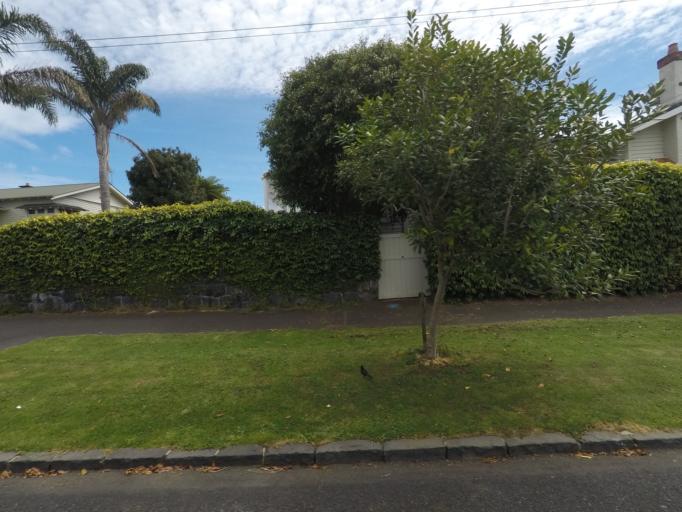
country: NZ
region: Auckland
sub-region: Auckland
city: Auckland
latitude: -36.8841
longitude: 174.7223
